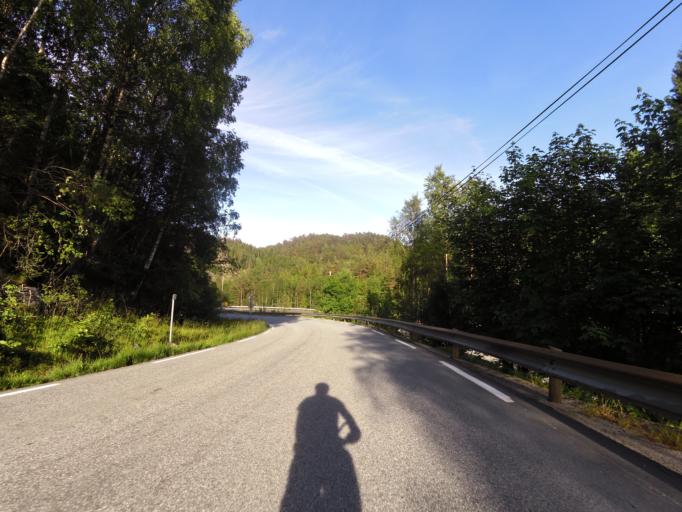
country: NO
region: Vest-Agder
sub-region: Flekkefjord
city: Flekkefjord
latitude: 58.2781
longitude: 6.6306
